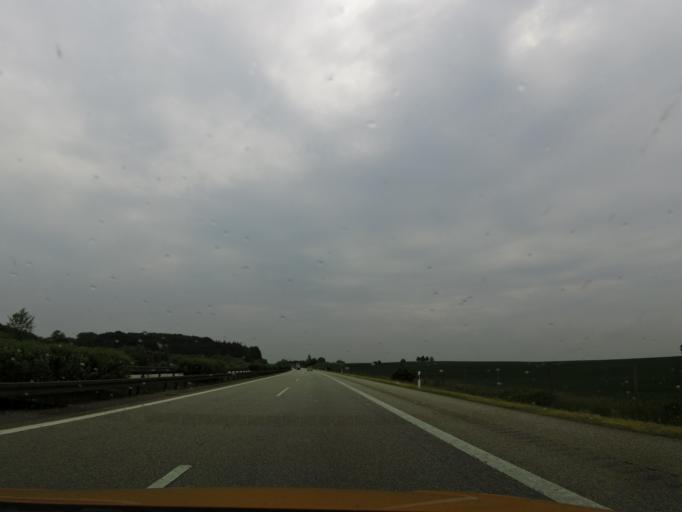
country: DE
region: Mecklenburg-Vorpommern
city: Rehna
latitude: 53.8191
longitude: 11.0953
